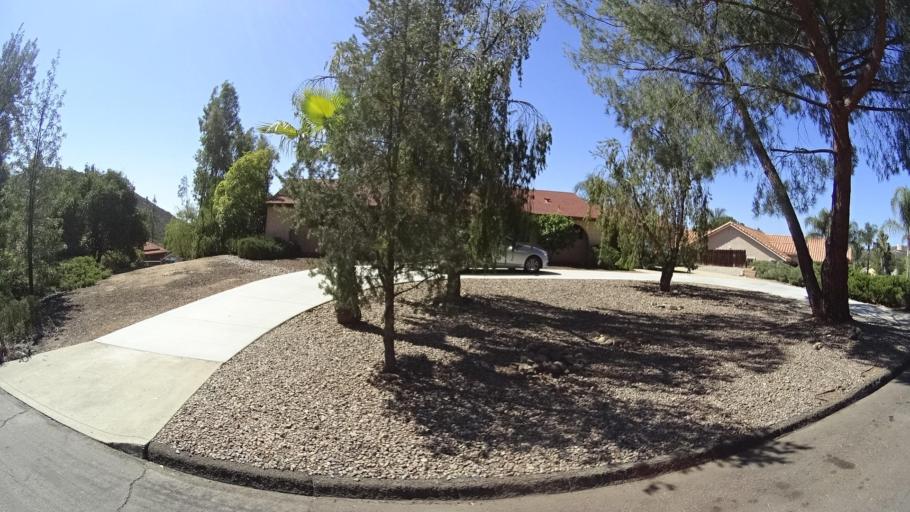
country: US
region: California
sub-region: San Diego County
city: San Diego Country Estates
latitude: 33.0265
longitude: -116.8002
